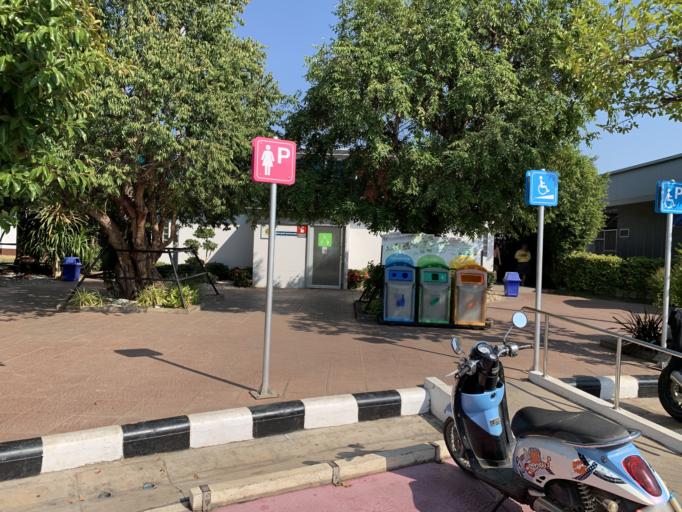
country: TH
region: Uttaradit
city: Nam Pat
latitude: 17.7273
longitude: 100.6771
